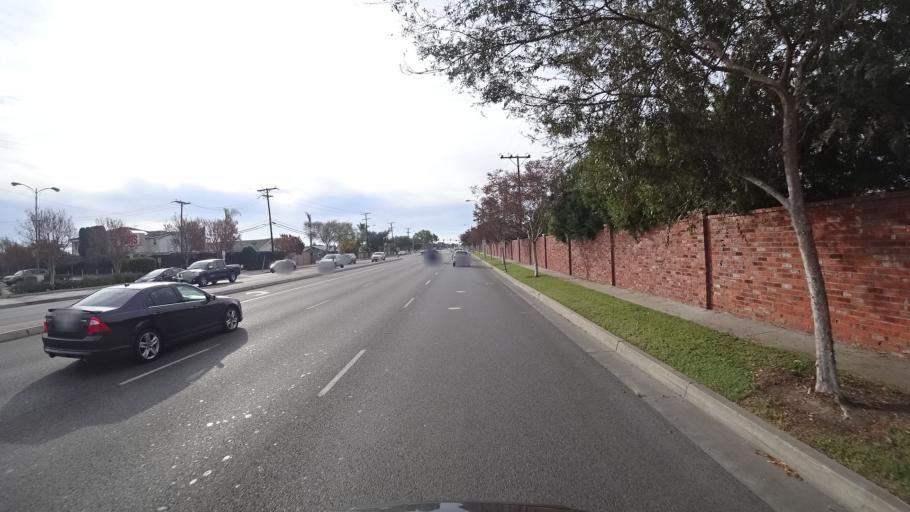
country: US
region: California
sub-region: Orange County
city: Los Alamitos
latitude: 33.7980
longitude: -118.0720
